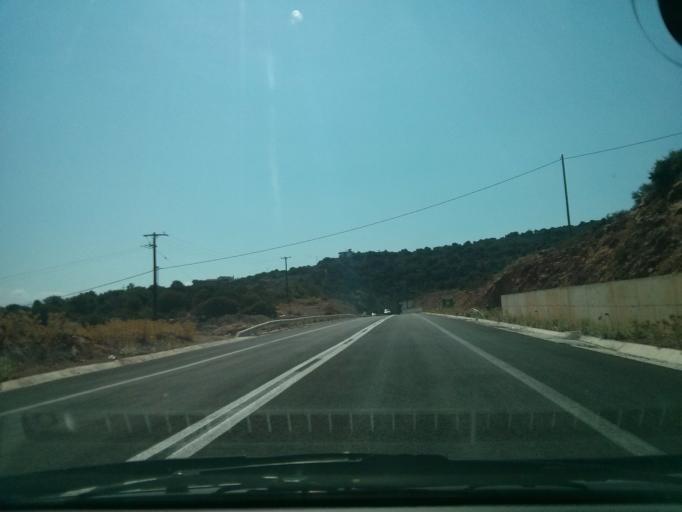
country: GR
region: Crete
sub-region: Nomos Lasithiou
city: Agios Nikolaos
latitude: 35.1638
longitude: 25.7050
